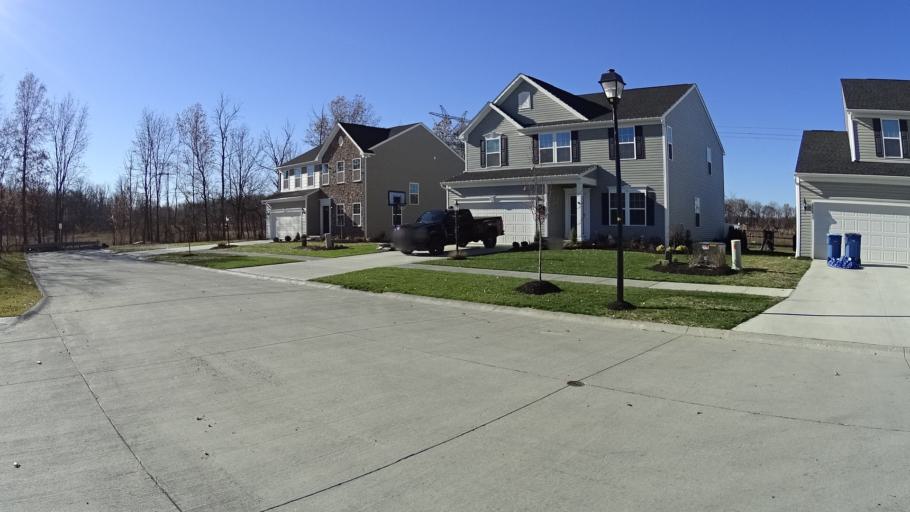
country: US
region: Ohio
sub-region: Lorain County
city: Avon
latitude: 41.4427
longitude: -82.0665
